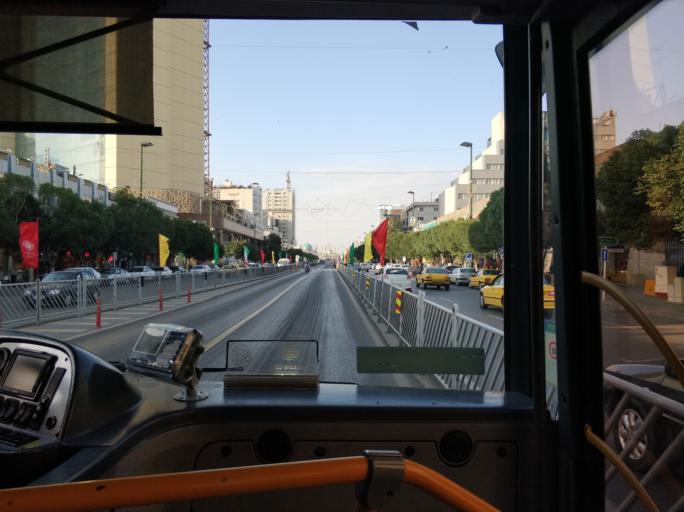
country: IR
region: Razavi Khorasan
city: Mashhad
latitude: 36.2796
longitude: 59.6087
